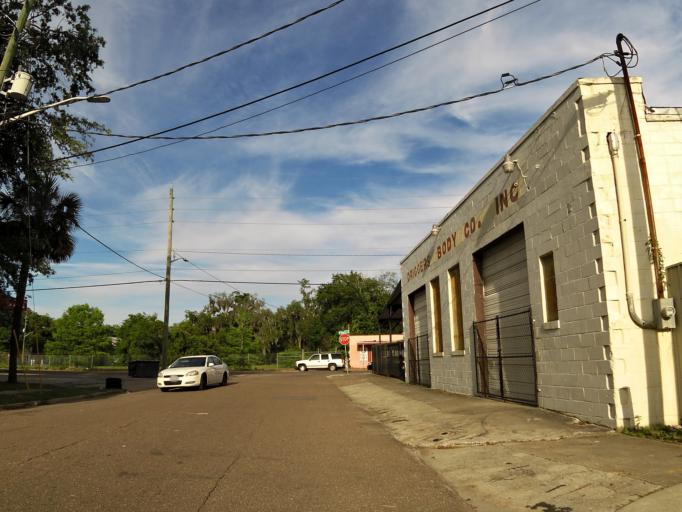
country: US
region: Florida
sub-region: Duval County
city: Jacksonville
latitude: 30.3606
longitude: -81.6581
